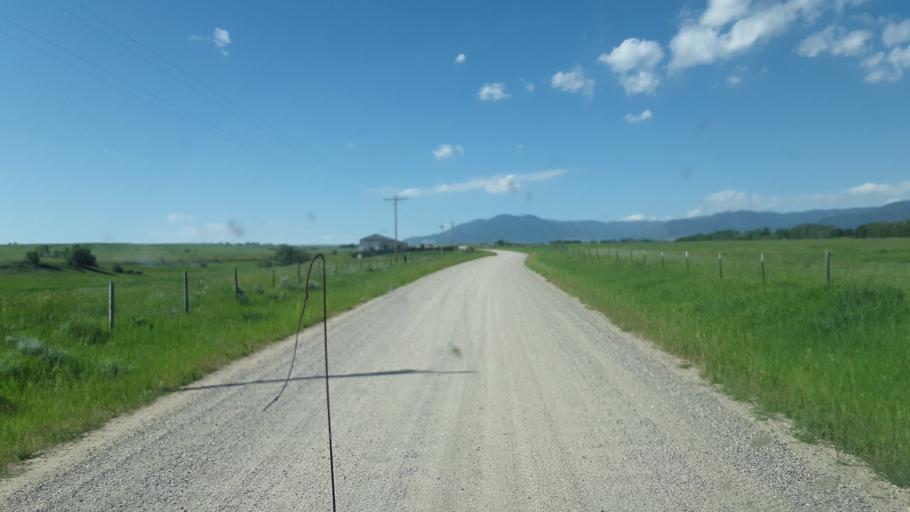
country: US
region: Montana
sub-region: Carbon County
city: Red Lodge
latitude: 45.2883
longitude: -109.1886
